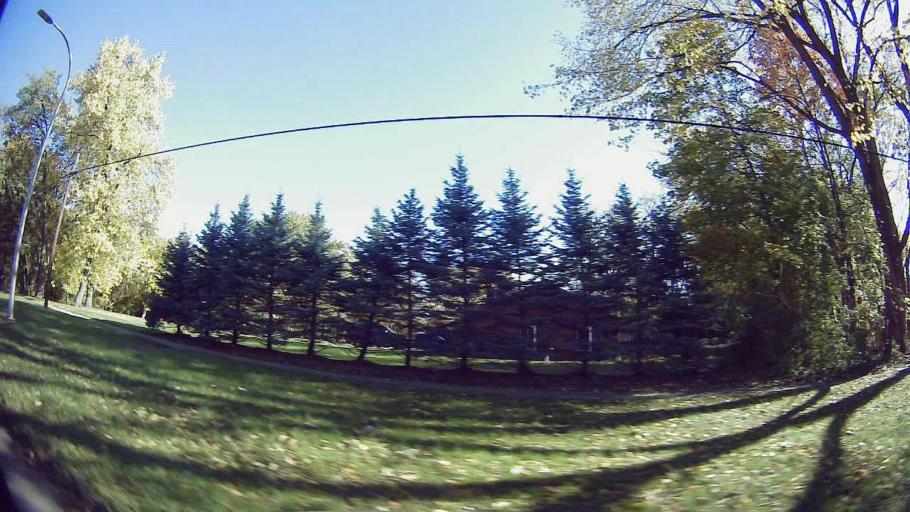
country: US
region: Michigan
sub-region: Wayne County
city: Livonia
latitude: 42.4053
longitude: -83.3738
